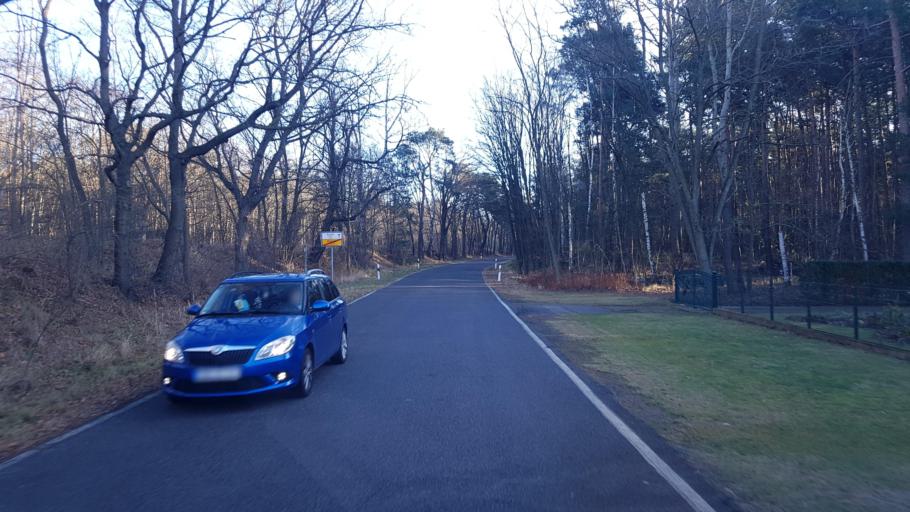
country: DE
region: Brandenburg
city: Heinersbruck
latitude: 51.7429
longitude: 14.5242
